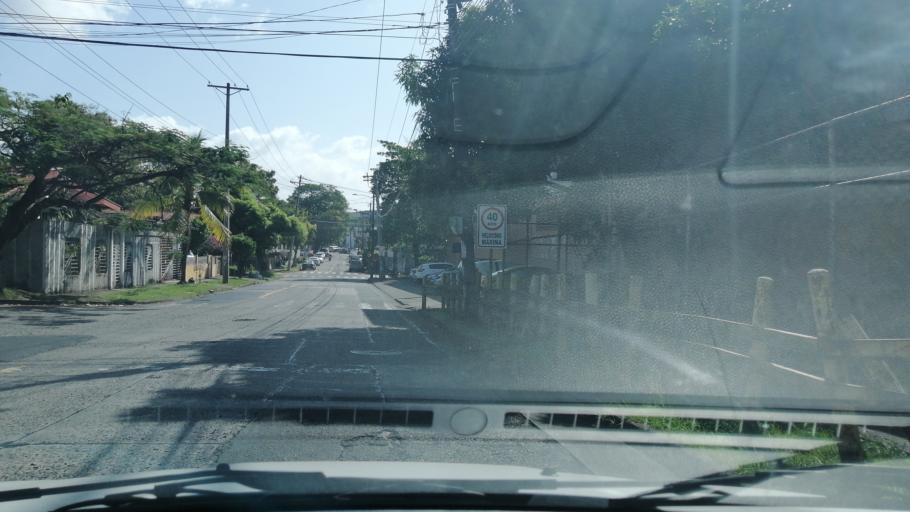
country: PA
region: Panama
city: Panama
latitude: 9.0070
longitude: -79.5317
